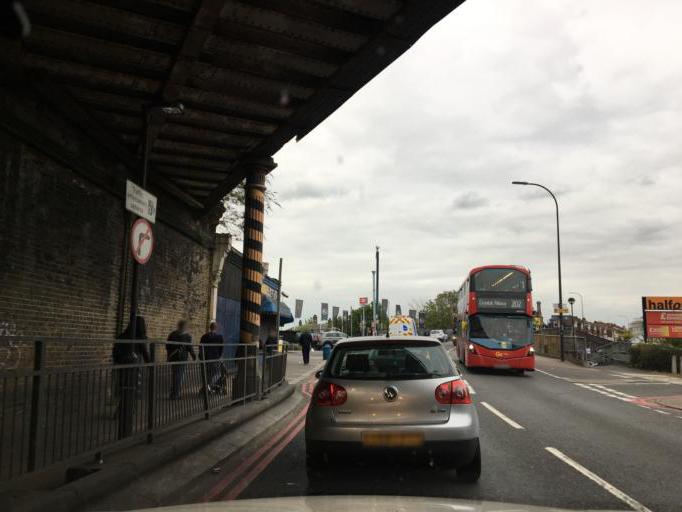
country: GB
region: England
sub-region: Greater London
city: Catford
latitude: 51.4437
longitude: -0.0265
